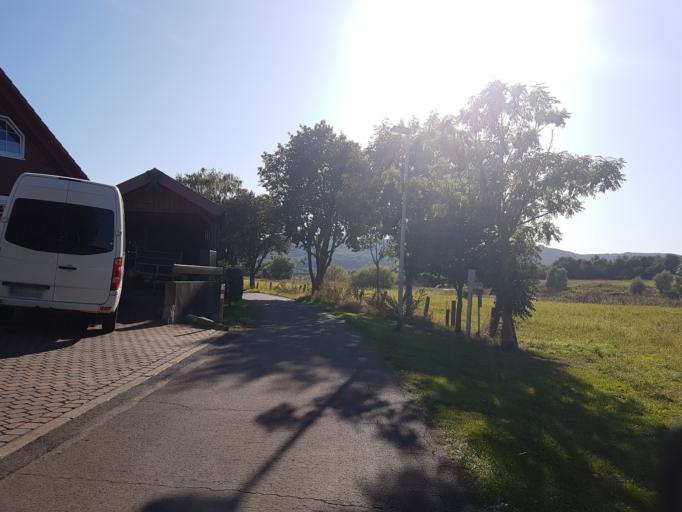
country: DE
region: North Rhine-Westphalia
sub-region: Regierungsbezirk Detmold
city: Minden
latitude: 52.2674
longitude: 8.9280
